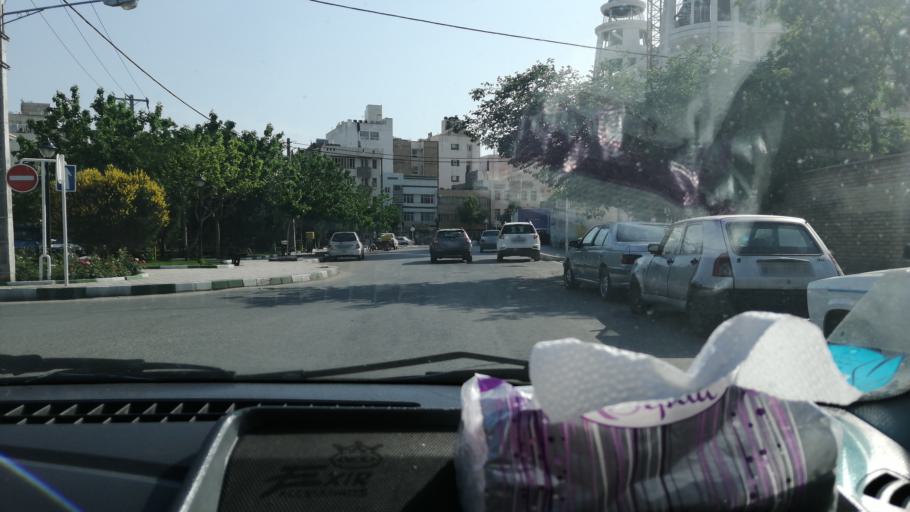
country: IR
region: Razavi Khorasan
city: Mashhad
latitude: 36.3123
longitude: 59.5619
